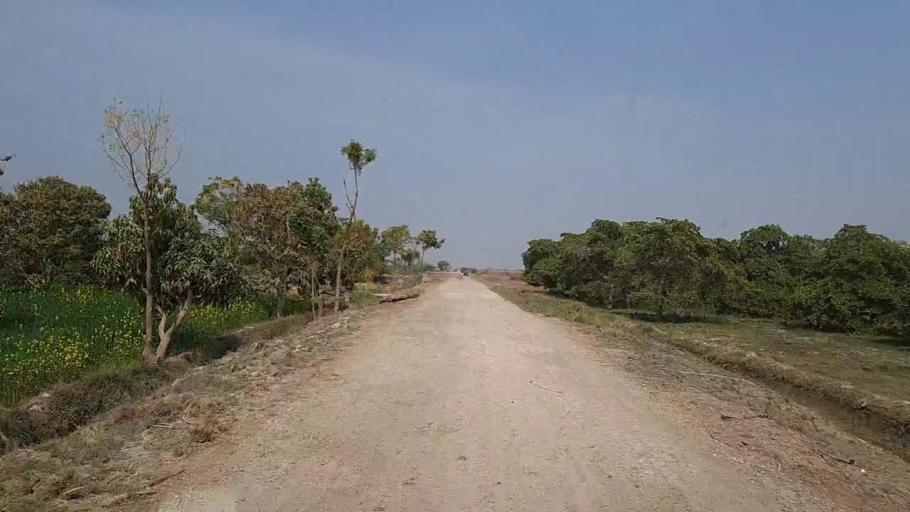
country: PK
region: Sindh
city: Mirwah Gorchani
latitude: 25.3477
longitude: 69.0637
